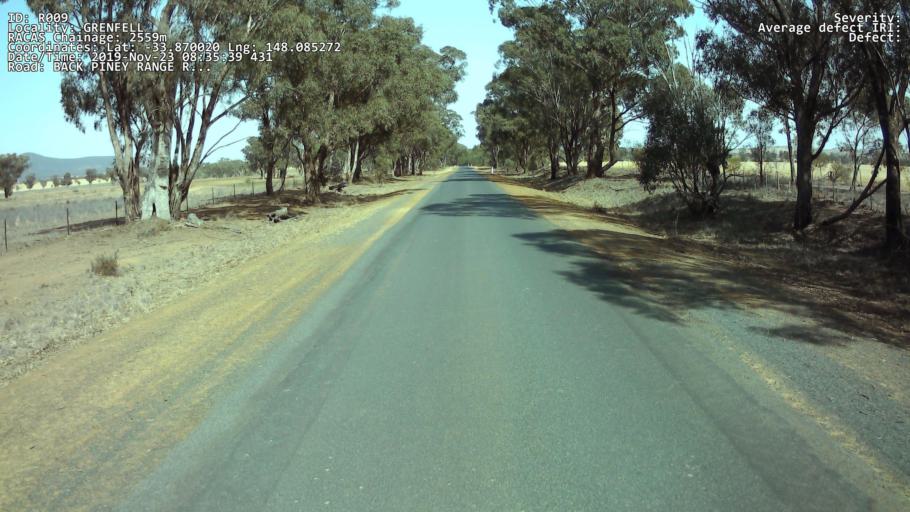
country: AU
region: New South Wales
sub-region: Weddin
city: Grenfell
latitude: -33.8700
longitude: 148.0852
